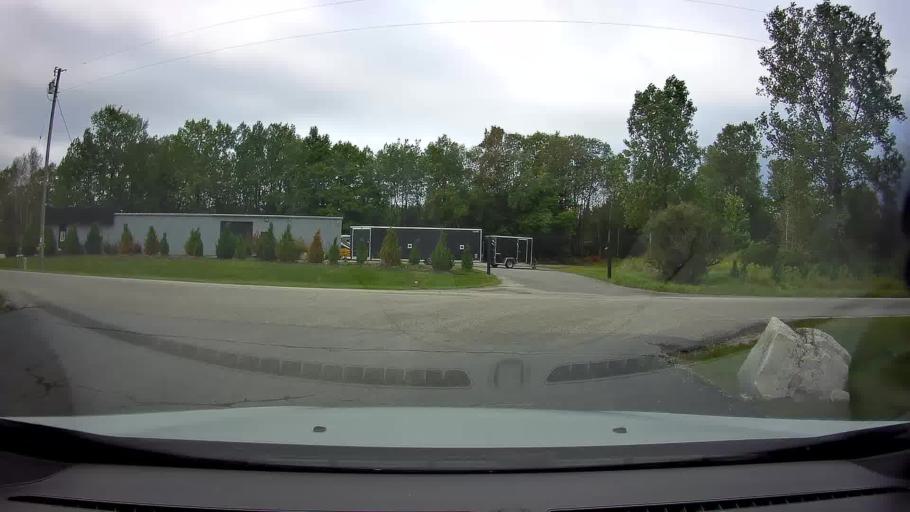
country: US
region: Wisconsin
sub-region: Door County
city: Sturgeon Bay
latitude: 44.8599
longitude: -87.3452
